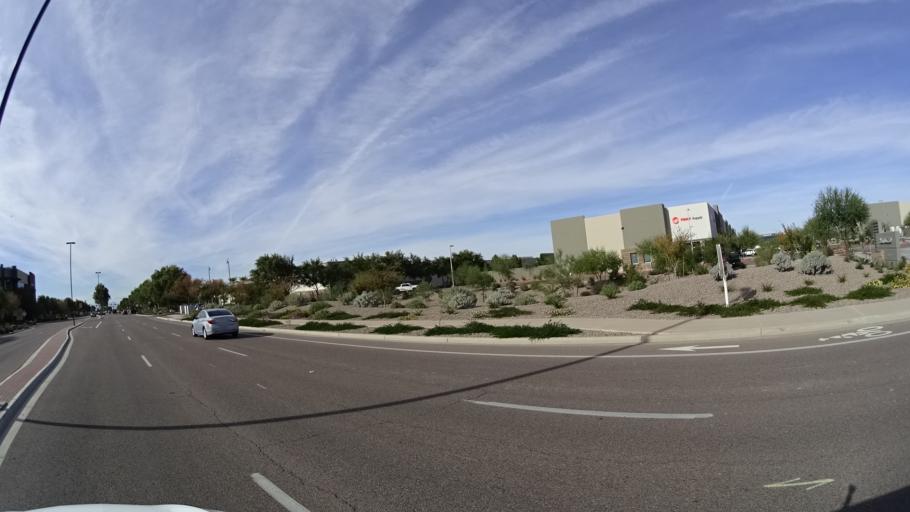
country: US
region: Arizona
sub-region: Maricopa County
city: Chandler
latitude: 33.2775
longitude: -111.7839
